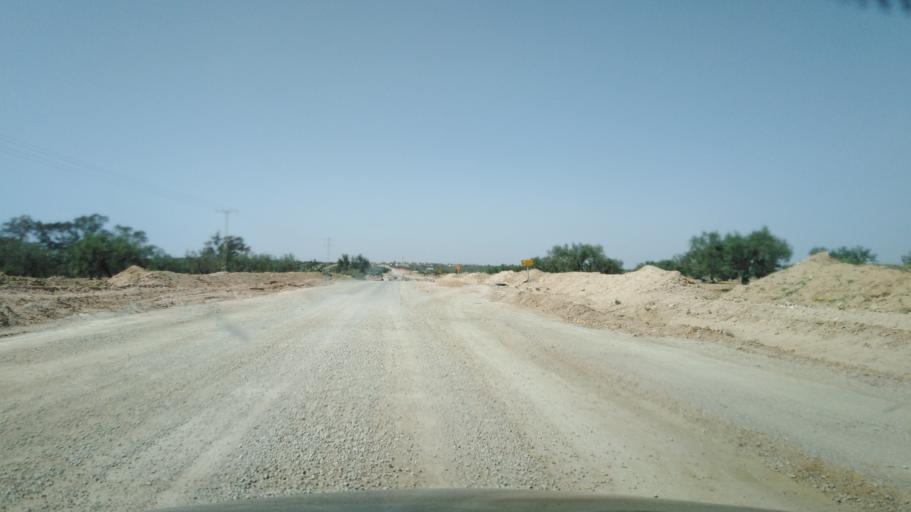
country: TN
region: Safaqis
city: Sfax
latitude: 34.6904
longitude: 10.4687
